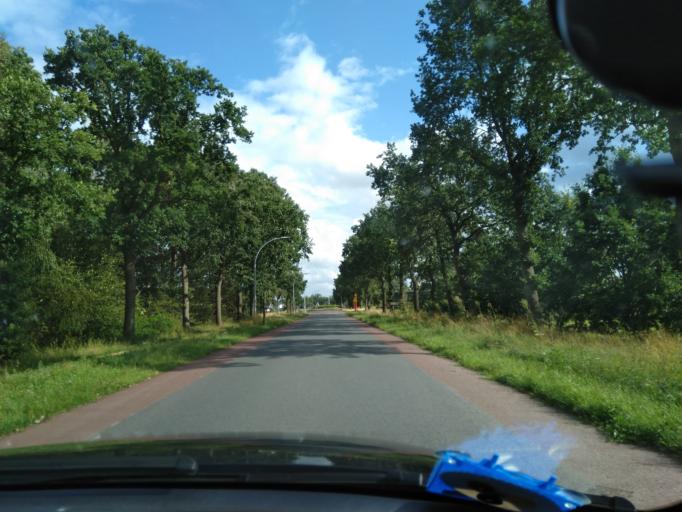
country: NL
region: Groningen
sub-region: Gemeente Zuidhorn
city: Zuidhorn
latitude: 53.2513
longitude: 6.4047
